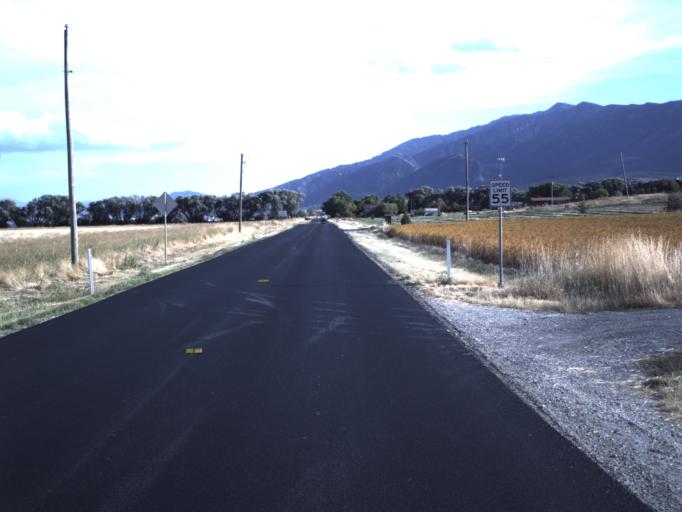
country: US
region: Utah
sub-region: Cache County
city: Mendon
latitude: 41.7493
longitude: -111.9794
